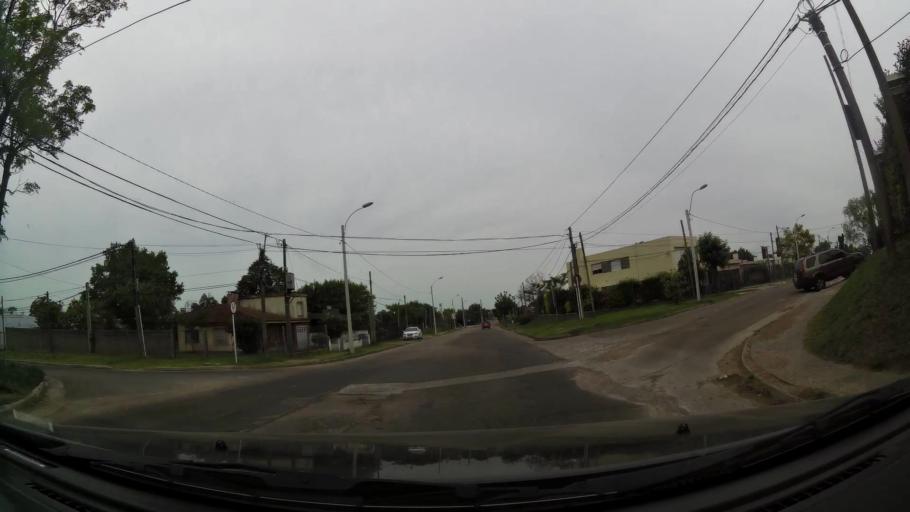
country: UY
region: Canelones
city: Las Piedras
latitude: -34.7329
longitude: -56.2152
